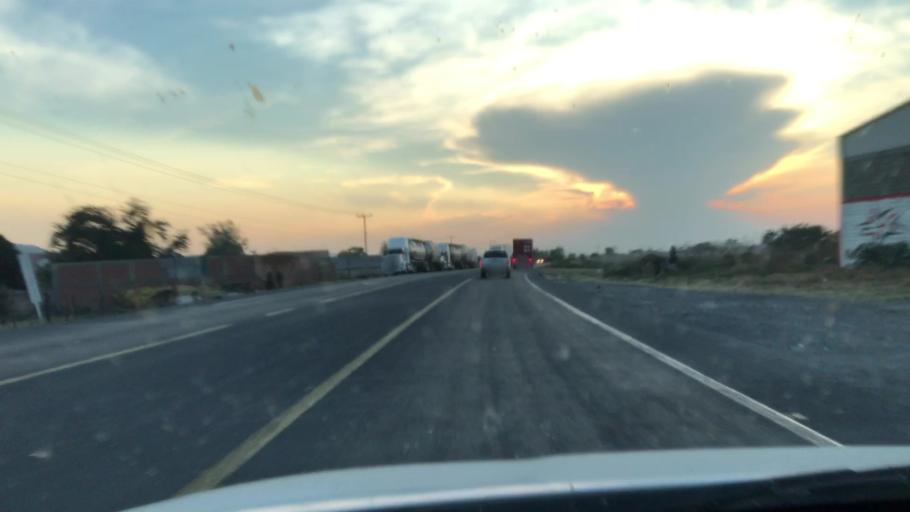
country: MX
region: Michoacan
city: Tanhuato de Guerrero
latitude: 20.2994
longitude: -102.3252
